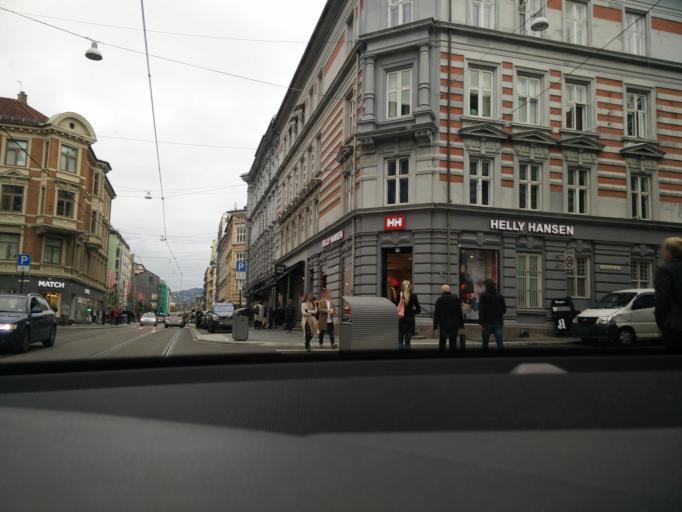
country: NO
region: Oslo
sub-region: Oslo
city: Oslo
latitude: 59.9256
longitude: 10.7228
